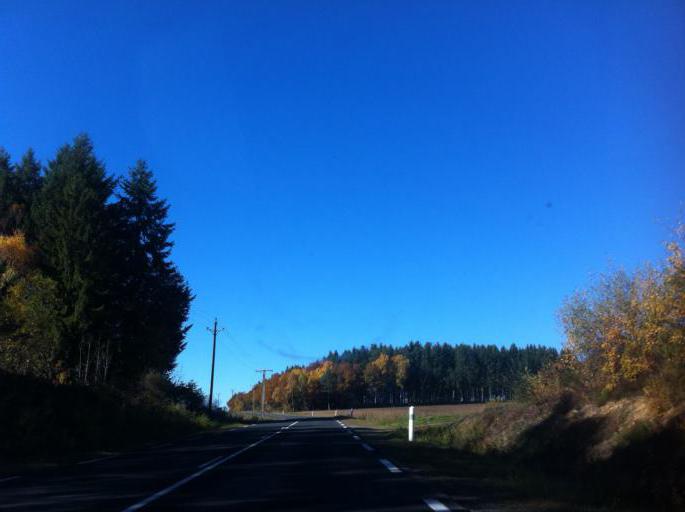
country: FR
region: Auvergne
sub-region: Departement du Puy-de-Dome
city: Gelles
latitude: 45.8635
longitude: 2.6579
